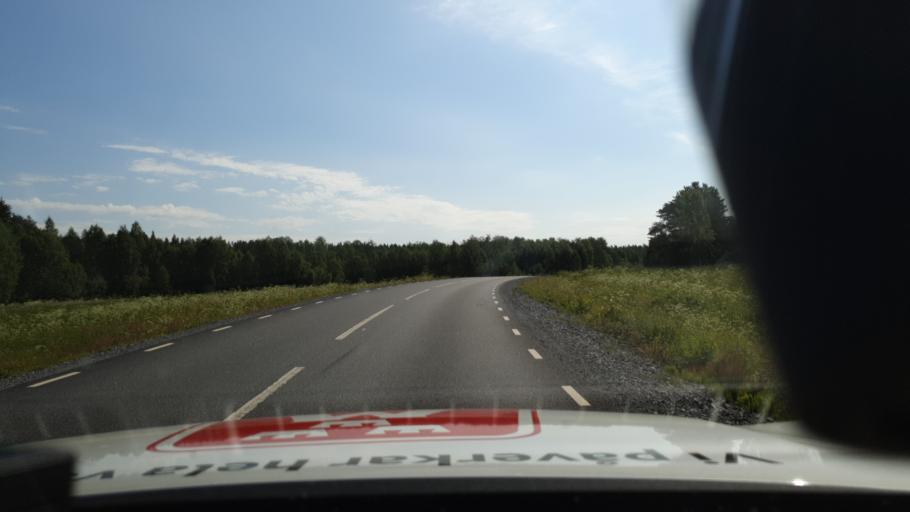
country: SE
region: Norrbotten
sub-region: Bodens Kommun
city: Saevast
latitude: 65.8444
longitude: 21.7892
